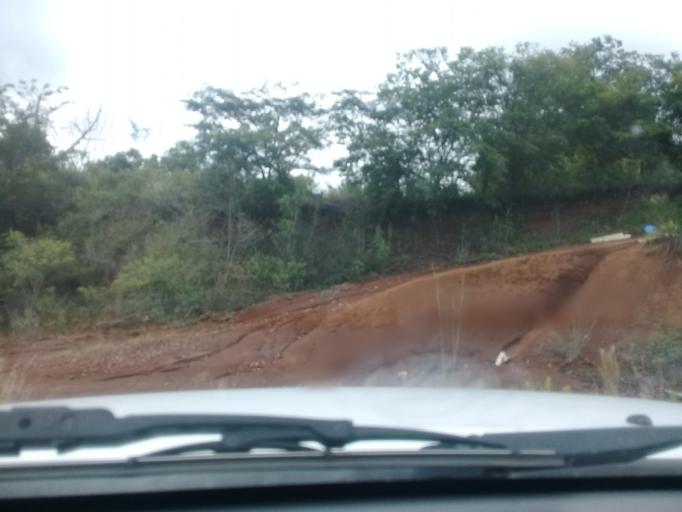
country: MX
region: Veracruz
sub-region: Xalapa
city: Lomas Verdes
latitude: 19.4990
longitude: -96.9139
